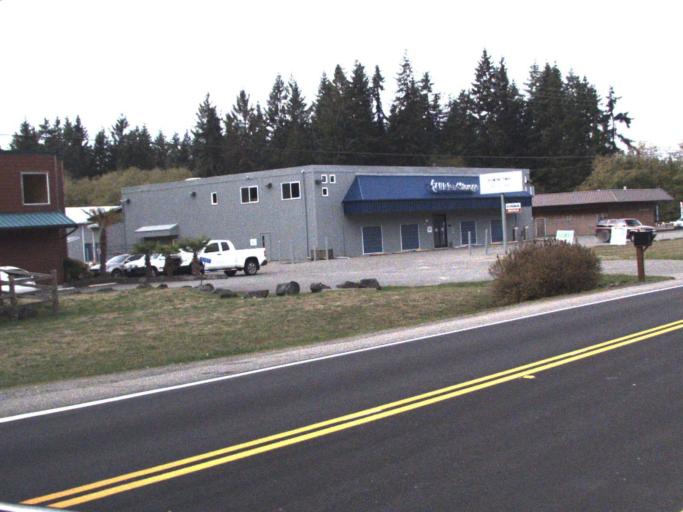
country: US
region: Washington
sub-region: Island County
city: Langley
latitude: 47.9919
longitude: -122.3972
